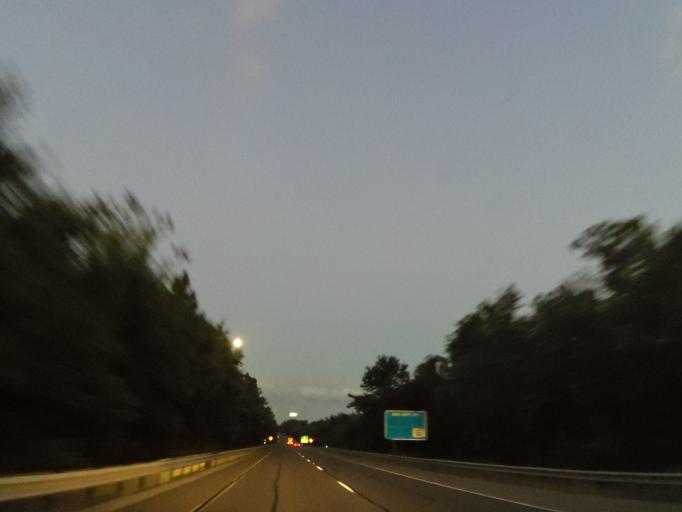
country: US
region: Tennessee
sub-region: Cumberland County
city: Crossville
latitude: 36.0114
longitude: -85.0645
